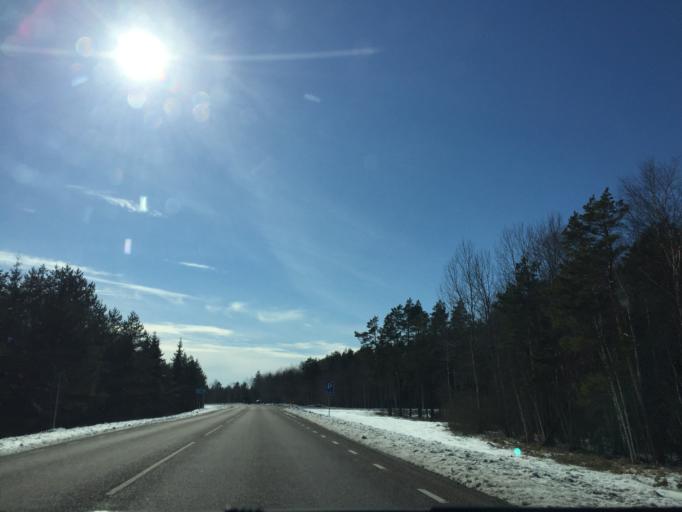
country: EE
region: Saare
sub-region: Kuressaare linn
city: Kuressaare
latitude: 58.3488
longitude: 22.6804
